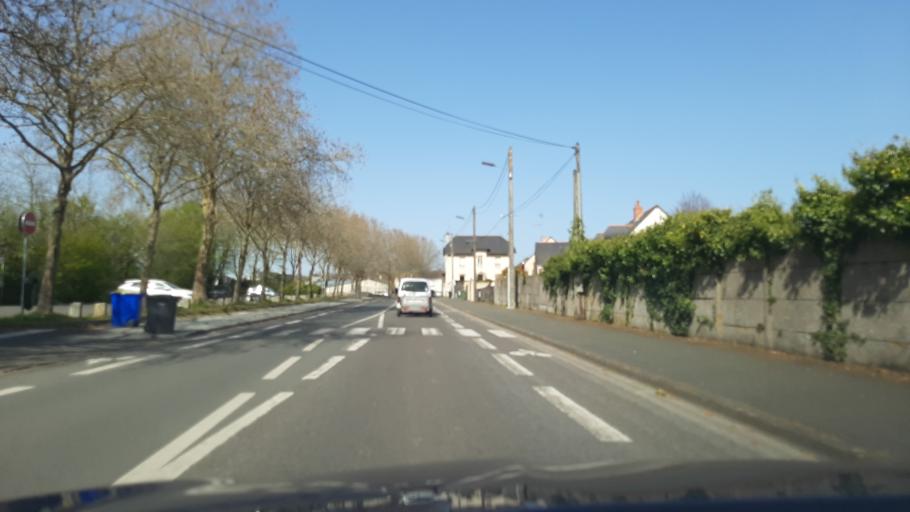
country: FR
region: Pays de la Loire
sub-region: Departement de Maine-et-Loire
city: Les Ponts-de-Ce
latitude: 47.4480
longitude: -0.5253
